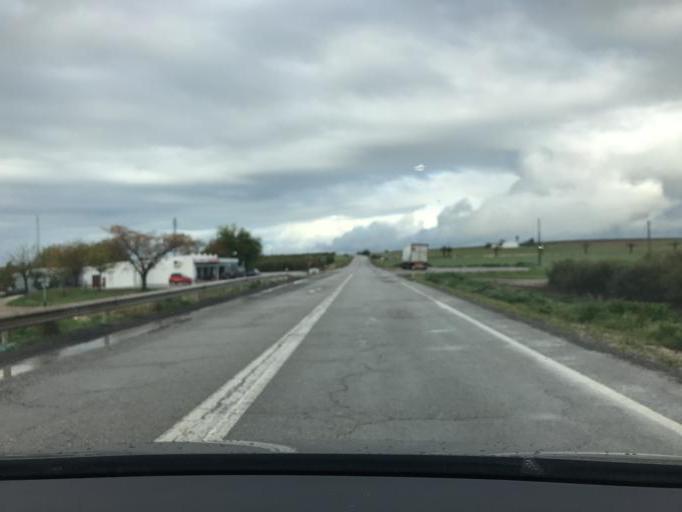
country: ES
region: Andalusia
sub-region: Provincia de Sevilla
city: La Luisiana
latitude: 37.4904
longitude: -5.1636
